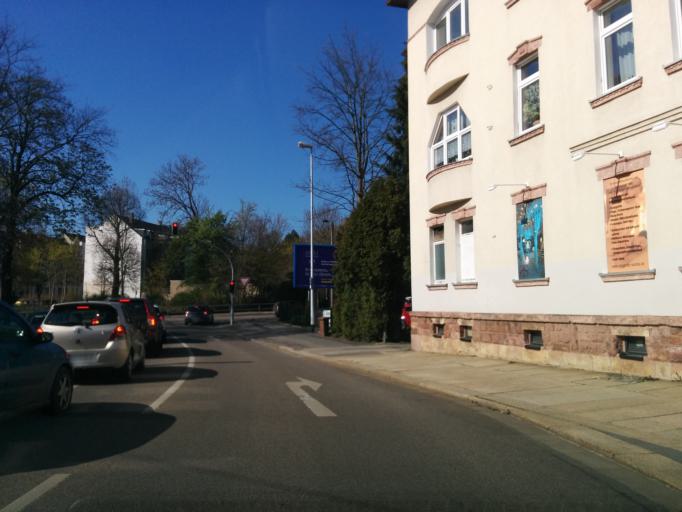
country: DE
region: Saxony
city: Hilbersdorf
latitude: 50.8309
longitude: 12.9550
